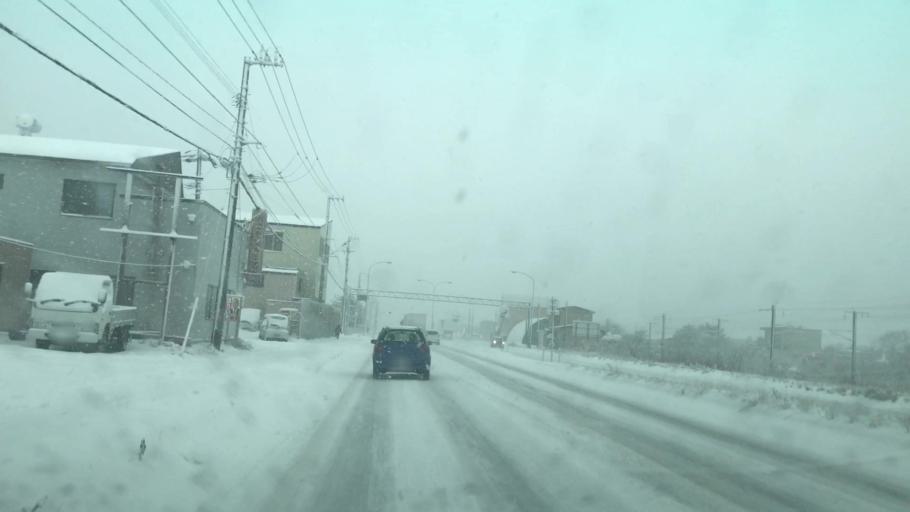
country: JP
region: Hokkaido
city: Muroran
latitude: 42.3858
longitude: 141.0783
